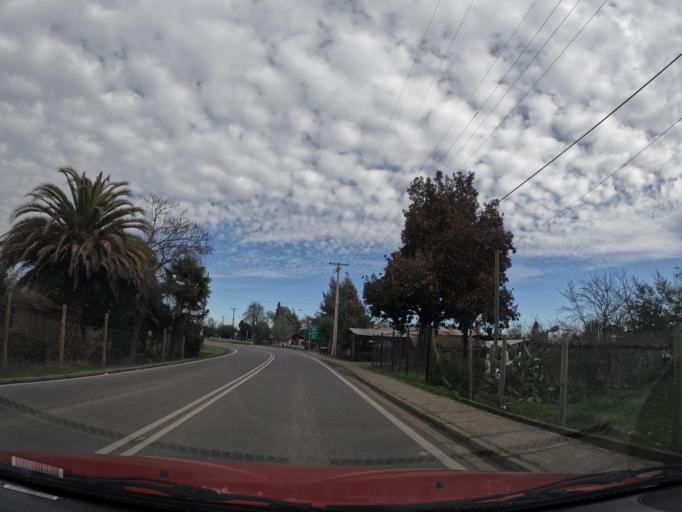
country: CL
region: Maule
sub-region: Provincia de Linares
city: Linares
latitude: -35.8799
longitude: -71.5436
